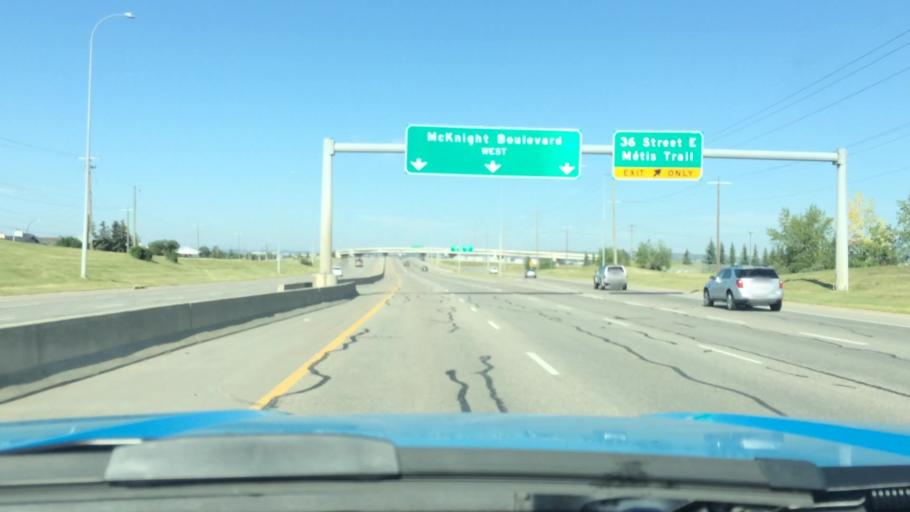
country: CA
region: Alberta
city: Calgary
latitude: 51.0961
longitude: -113.9731
